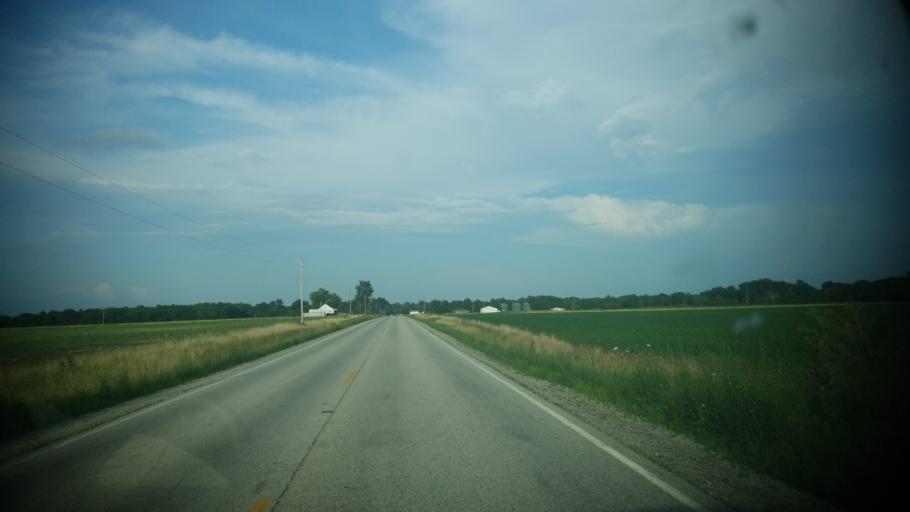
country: US
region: Illinois
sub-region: Clay County
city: Flora
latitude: 38.5161
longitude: -88.4568
